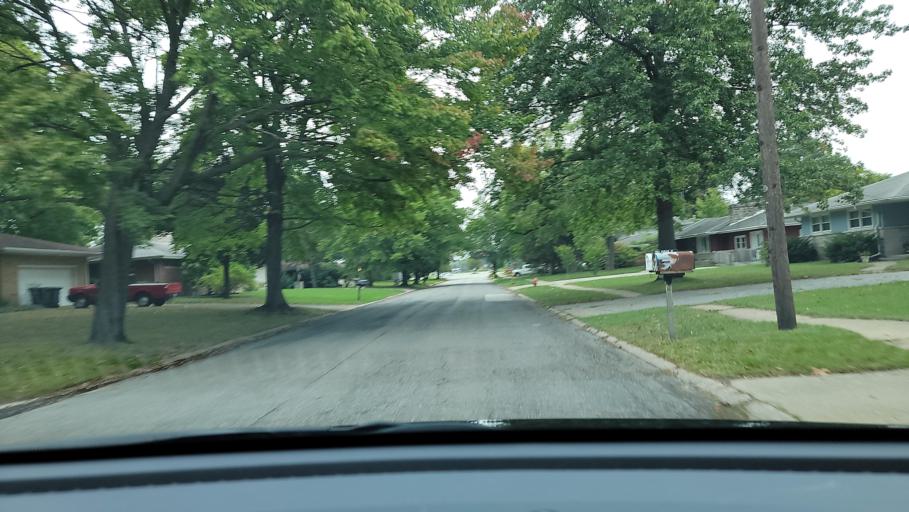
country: US
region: Indiana
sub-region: Porter County
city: Portage
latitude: 41.5741
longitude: -87.1763
